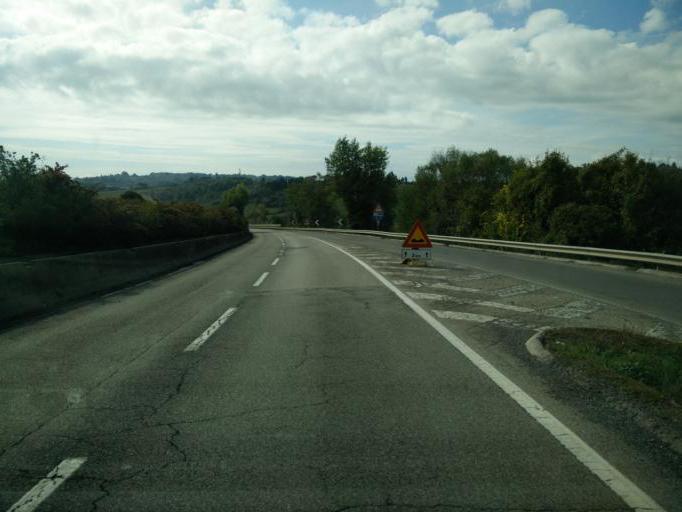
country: IT
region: Tuscany
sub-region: Provincia di Siena
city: Belverde
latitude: 43.3355
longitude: 11.2918
